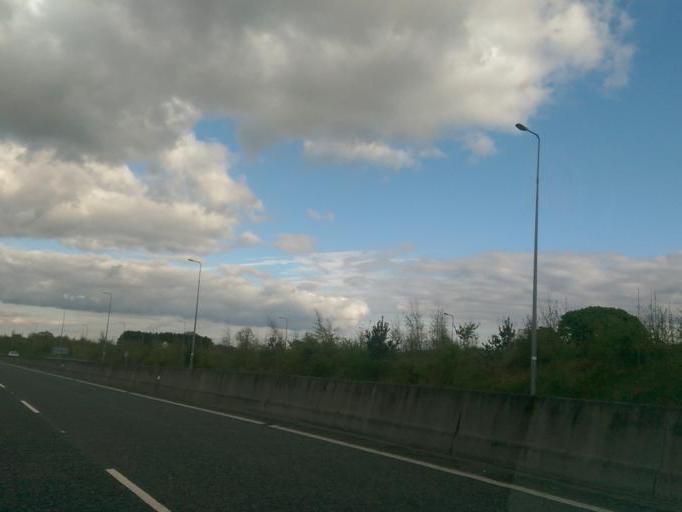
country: IE
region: Leinster
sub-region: An Iarmhi
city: Kilbeggan
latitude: 53.3583
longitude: -7.4910
